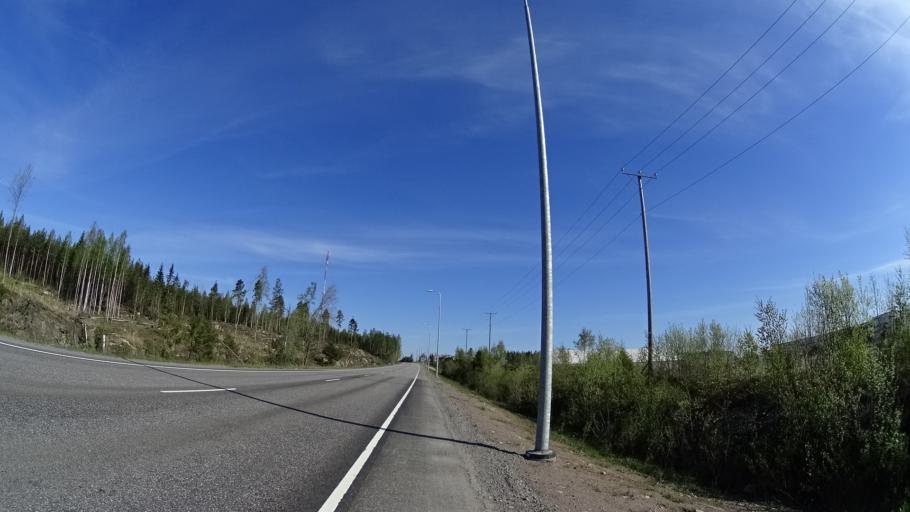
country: FI
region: Uusimaa
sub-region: Helsinki
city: Nurmijaervi
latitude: 60.4482
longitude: 24.8336
